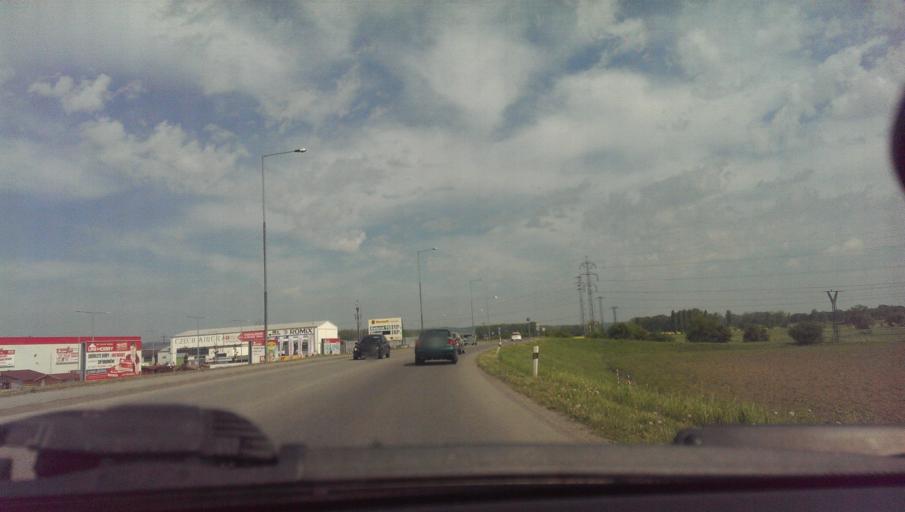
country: CZ
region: Zlin
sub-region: Okres Uherske Hradiste
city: Uherske Hradiste
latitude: 49.0785
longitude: 17.4539
